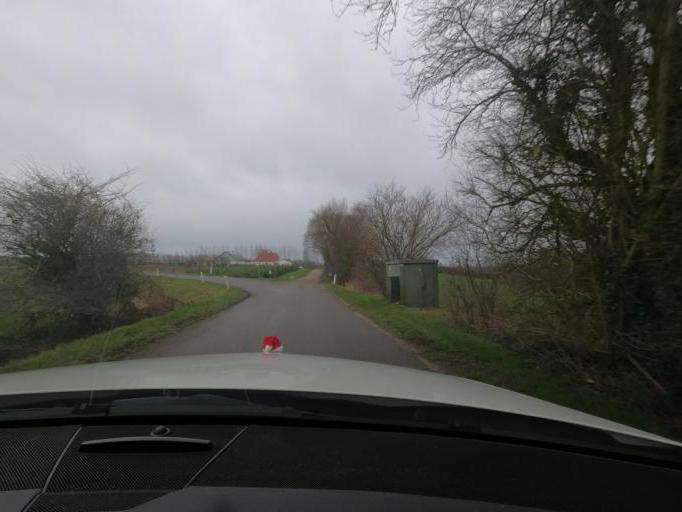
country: DK
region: South Denmark
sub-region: Haderslev Kommune
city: Starup
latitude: 55.2385
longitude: 9.7008
